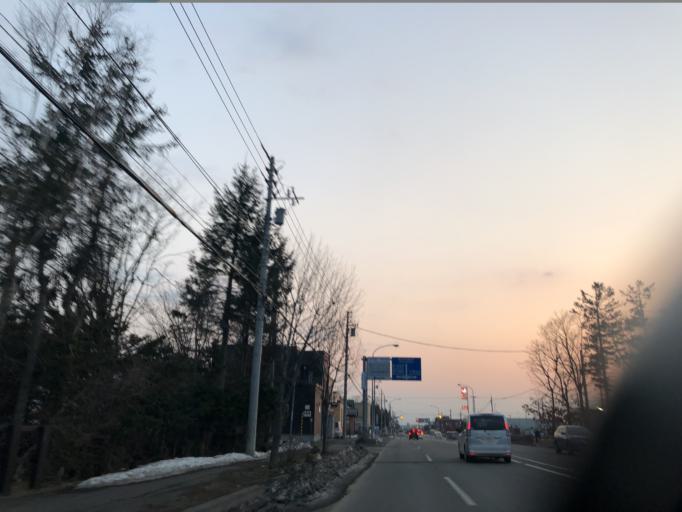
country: JP
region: Hokkaido
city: Chitose
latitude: 42.8265
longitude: 141.6716
